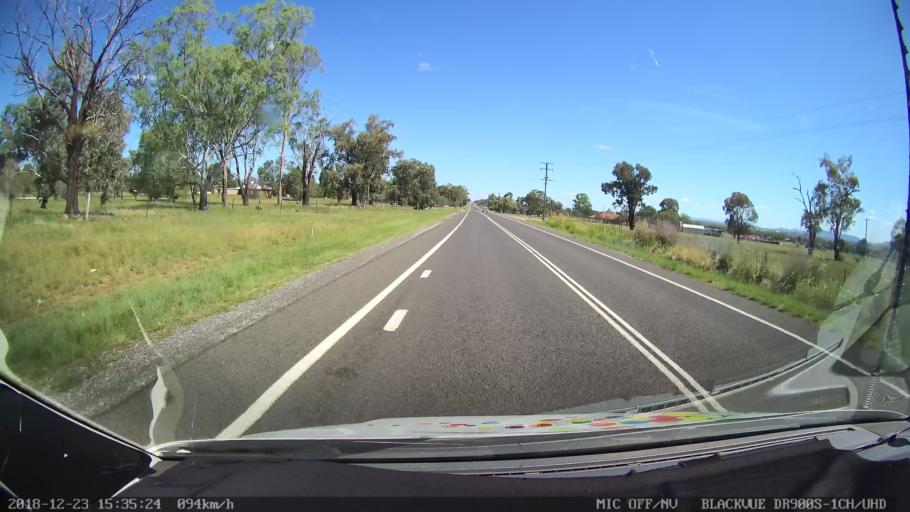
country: AU
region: New South Wales
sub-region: Tamworth Municipality
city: Tamworth
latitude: -31.0268
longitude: 150.8823
